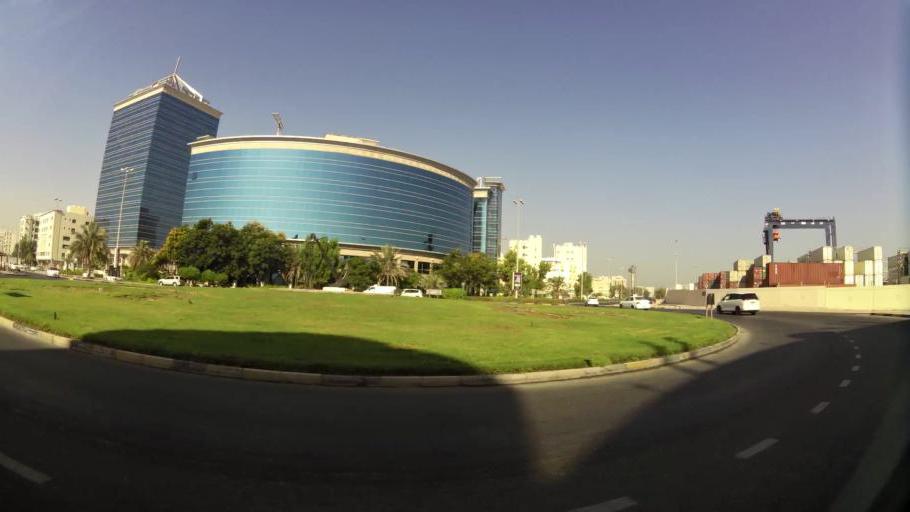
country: AE
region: Ajman
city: Ajman
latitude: 25.4200
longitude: 55.4538
